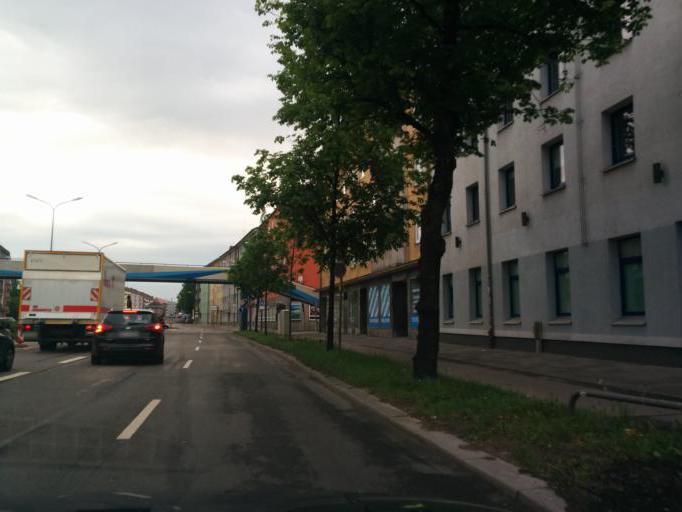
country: DE
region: Bavaria
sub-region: Upper Bavaria
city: Munich
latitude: 48.1073
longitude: 11.5798
